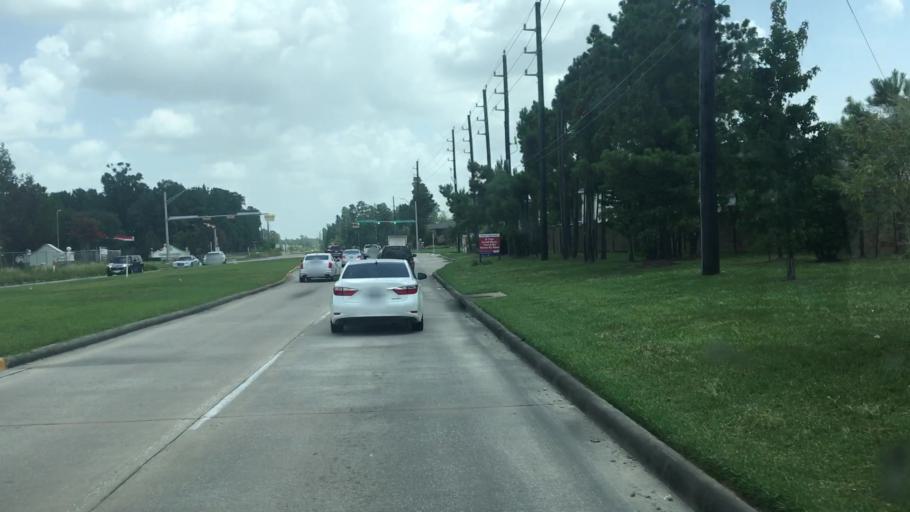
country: US
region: Texas
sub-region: Harris County
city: Atascocita
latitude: 29.9368
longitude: -95.1759
